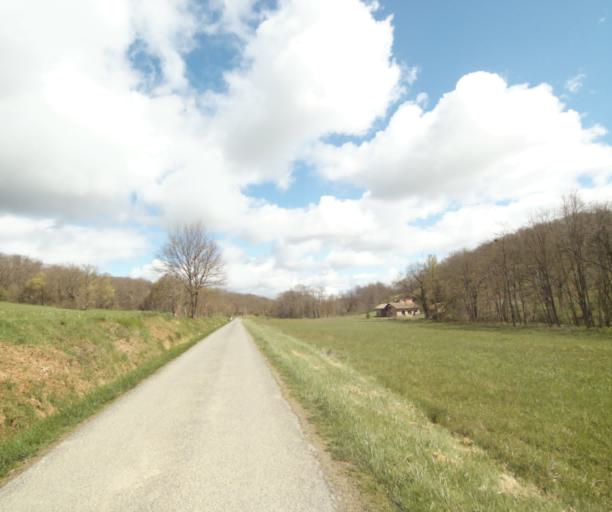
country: FR
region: Midi-Pyrenees
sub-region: Departement de l'Ariege
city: Saverdun
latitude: 43.1788
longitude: 1.5516
